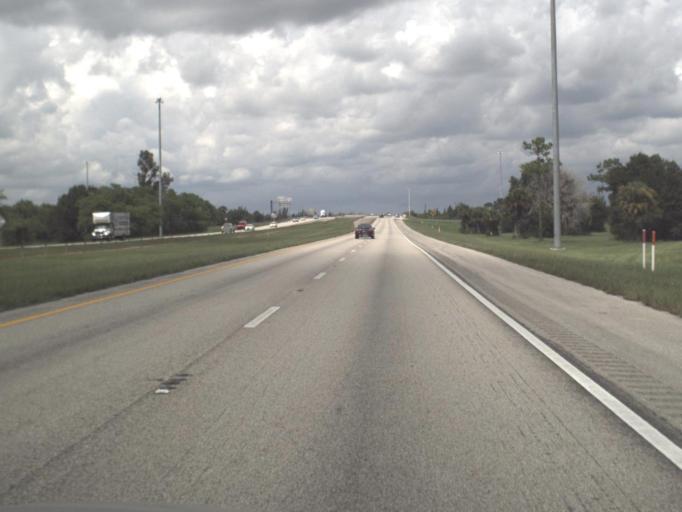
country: US
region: Florida
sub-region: Charlotte County
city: Punta Gorda
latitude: 26.9363
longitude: -82.0176
